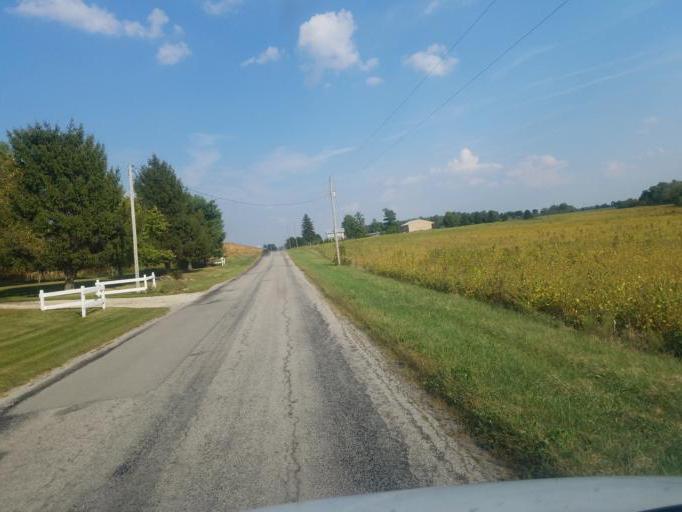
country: US
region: Ohio
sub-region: Hardin County
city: Forest
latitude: 40.9052
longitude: -83.5205
